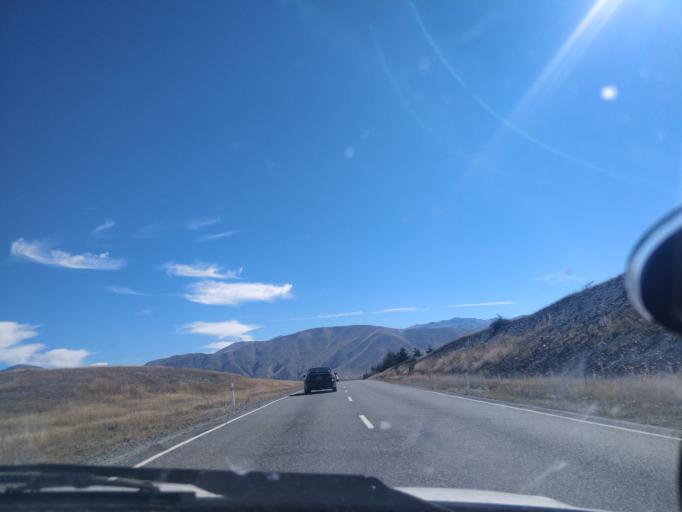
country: NZ
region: Otago
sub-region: Queenstown-Lakes District
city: Wanaka
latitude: -44.2715
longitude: 170.0464
